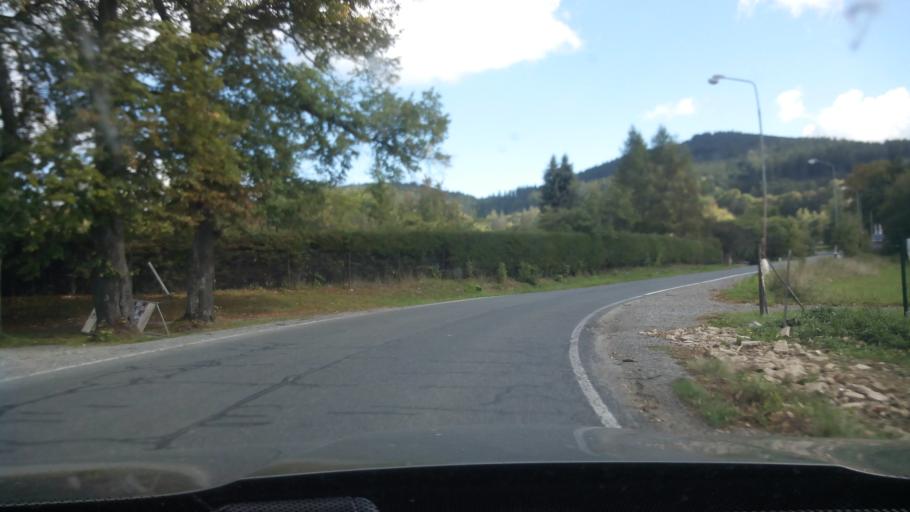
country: CZ
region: Plzensky
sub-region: Okres Klatovy
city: Kasperske Hory
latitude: 49.1468
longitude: 13.5666
